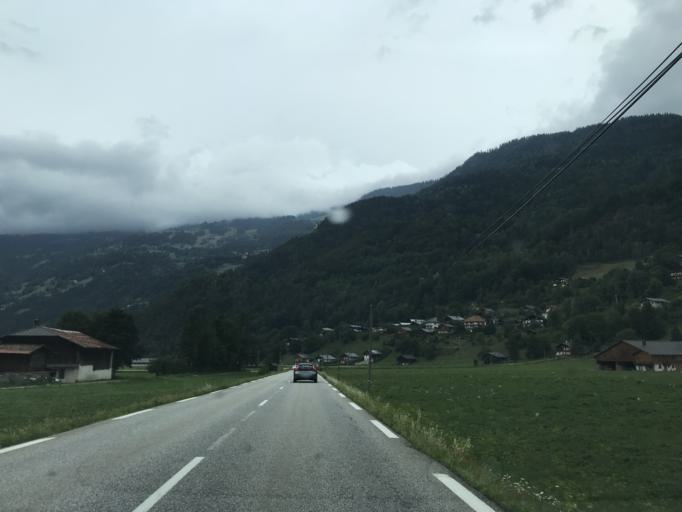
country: FR
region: Rhone-Alpes
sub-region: Departement de la Savoie
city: Beaufort
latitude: 45.7226
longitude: 6.5561
